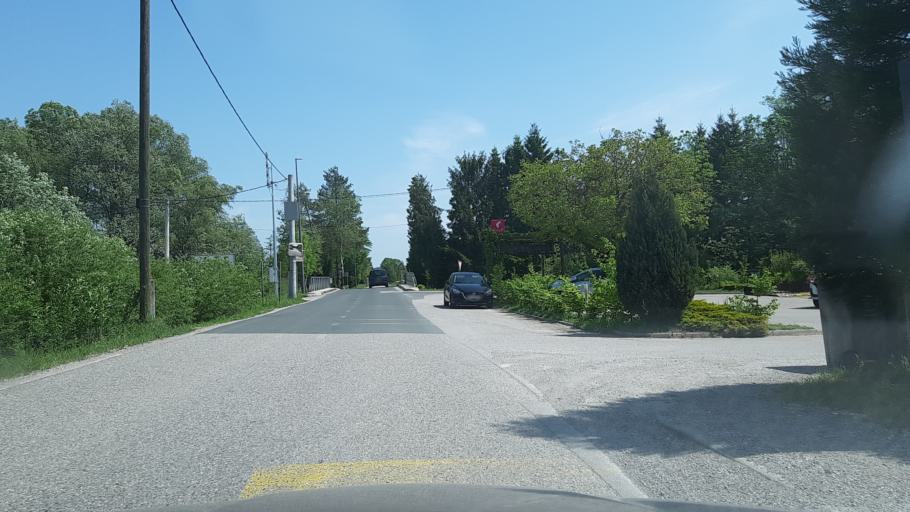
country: SI
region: Brezovica
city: Vnanje Gorice
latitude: 45.9974
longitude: 14.4701
